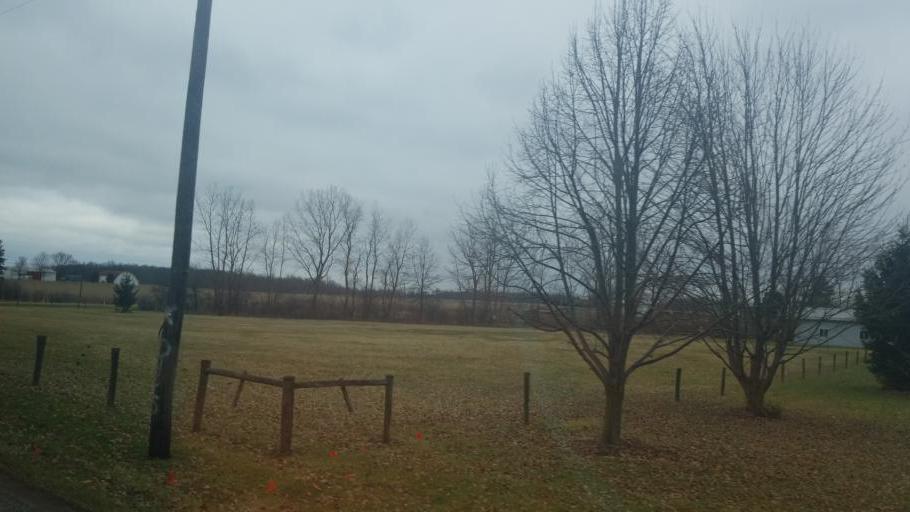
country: US
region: Ohio
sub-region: Crawford County
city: Crestline
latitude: 40.7977
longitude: -82.7170
